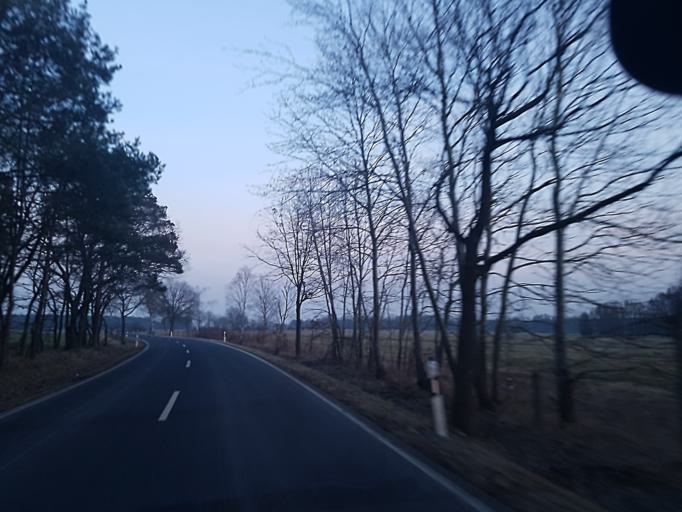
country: DE
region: Saxony-Anhalt
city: Holzdorf
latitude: 51.7507
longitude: 13.1478
